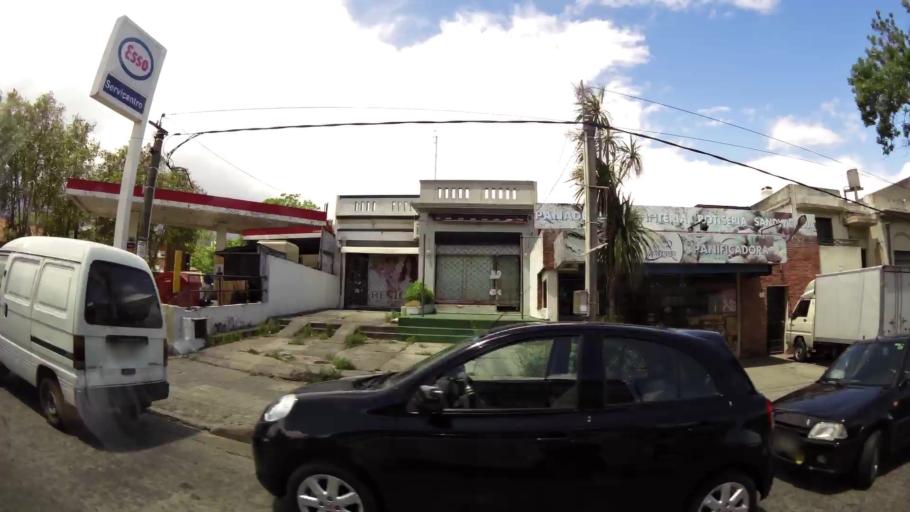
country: UY
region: Montevideo
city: Montevideo
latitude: -34.8614
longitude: -56.1863
